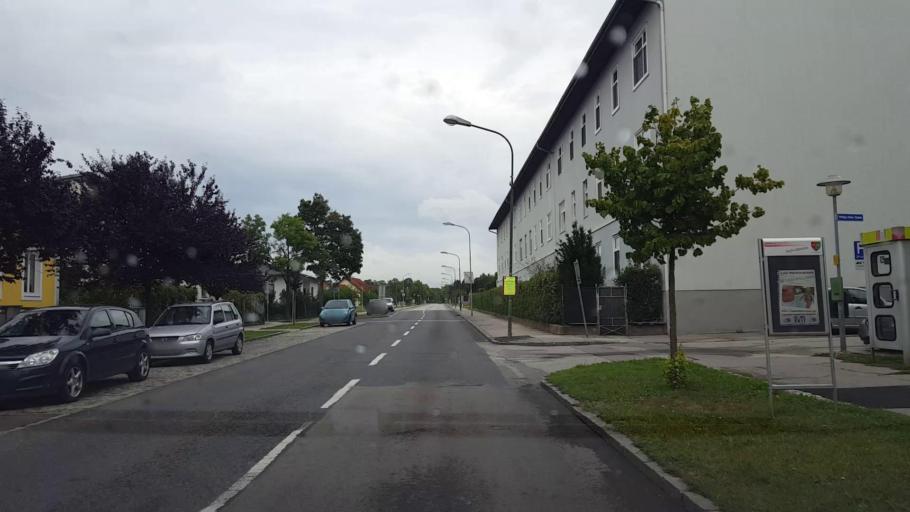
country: AT
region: Lower Austria
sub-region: Politischer Bezirk Wien-Umgebung
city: Ebergassing
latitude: 48.0474
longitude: 16.5159
